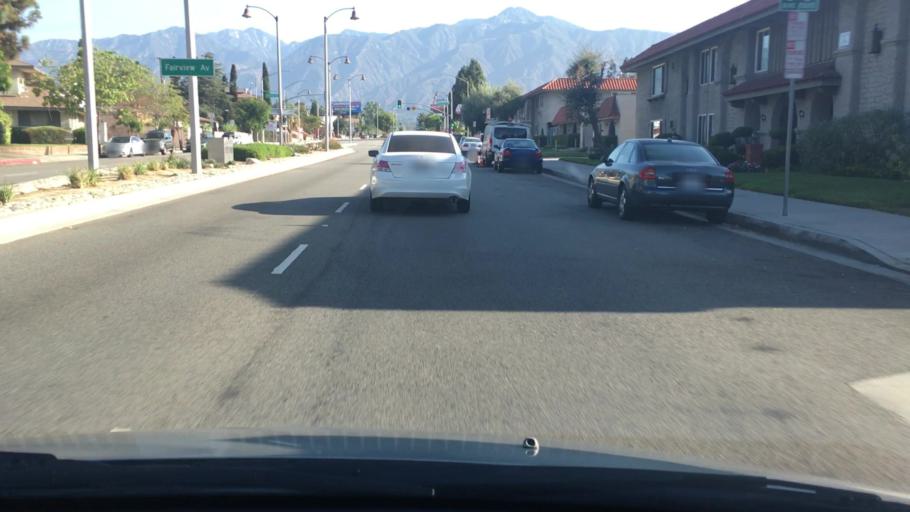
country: US
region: California
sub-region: Los Angeles County
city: Temple City
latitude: 34.1265
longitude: -118.0731
